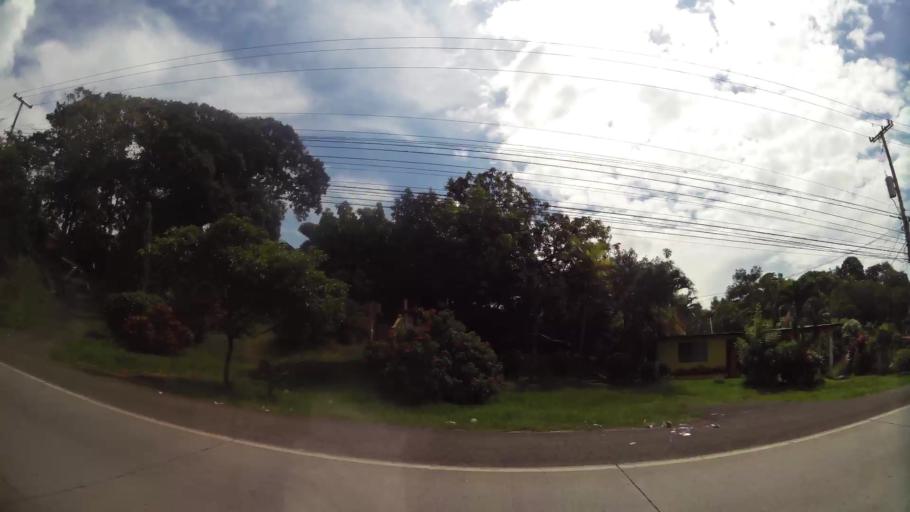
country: PA
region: Panama
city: Vista Alegre
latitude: 8.9396
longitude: -79.6804
